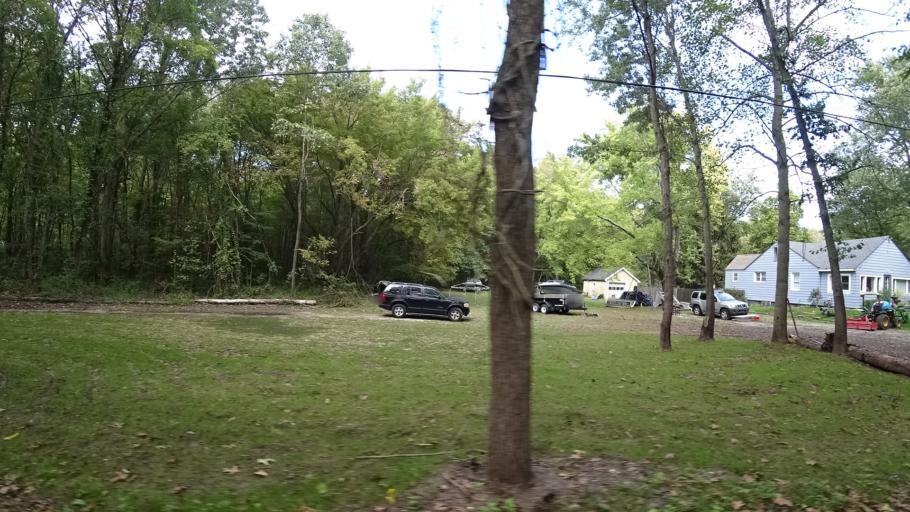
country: US
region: Indiana
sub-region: LaPorte County
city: Long Beach
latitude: 41.7276
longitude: -86.8483
